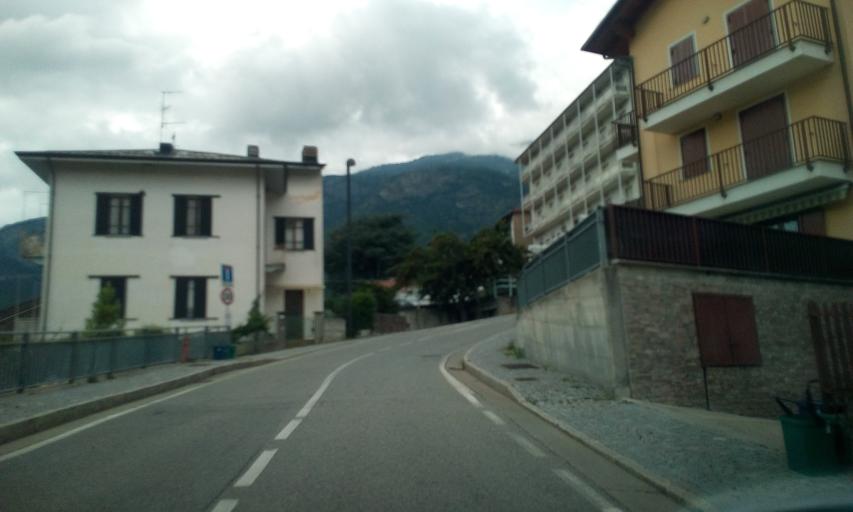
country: IT
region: Aosta Valley
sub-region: Valle d'Aosta
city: Saint-Vincent
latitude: 45.7471
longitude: 7.6526
